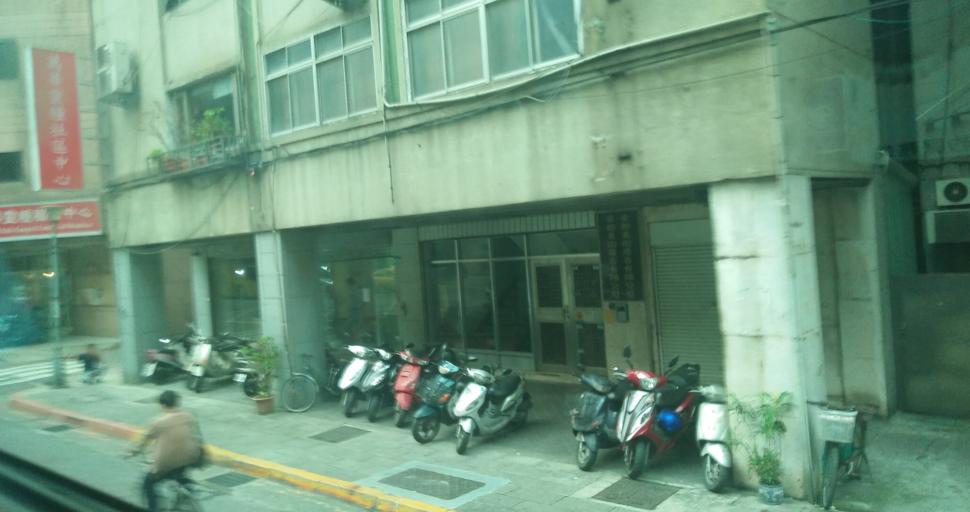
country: TW
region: Taipei
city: Taipei
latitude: 25.0378
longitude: 121.5050
